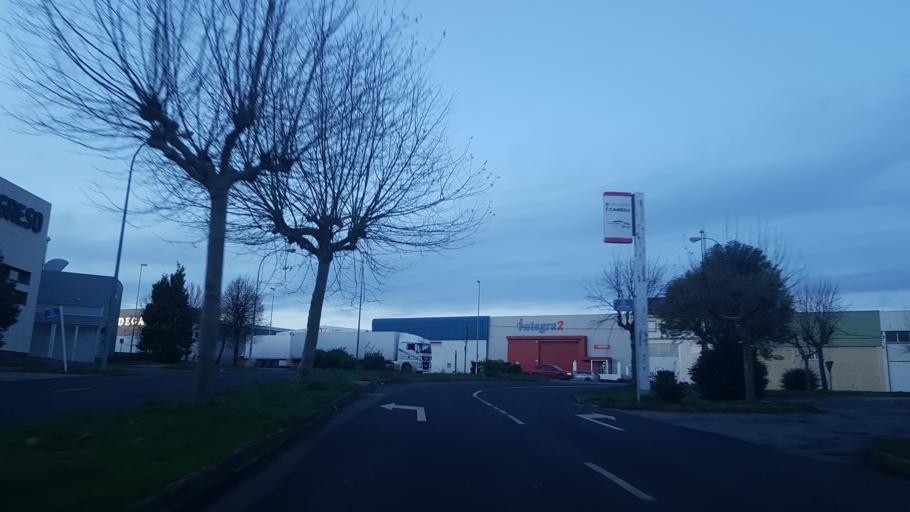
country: ES
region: Galicia
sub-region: Provincia de Lugo
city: Lugo
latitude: 43.0466
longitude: -7.5713
